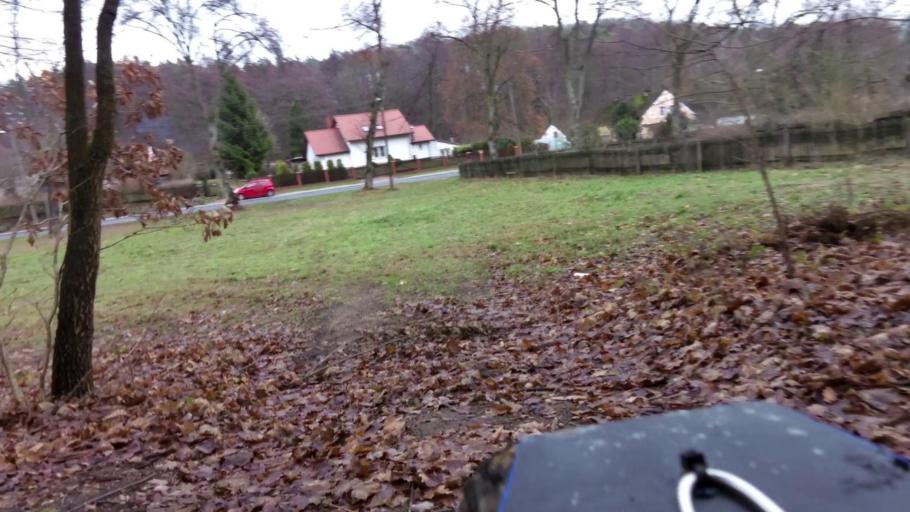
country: PL
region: Lubusz
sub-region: Powiat gorzowski
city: Bogdaniec
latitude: 52.6944
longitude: 15.0649
